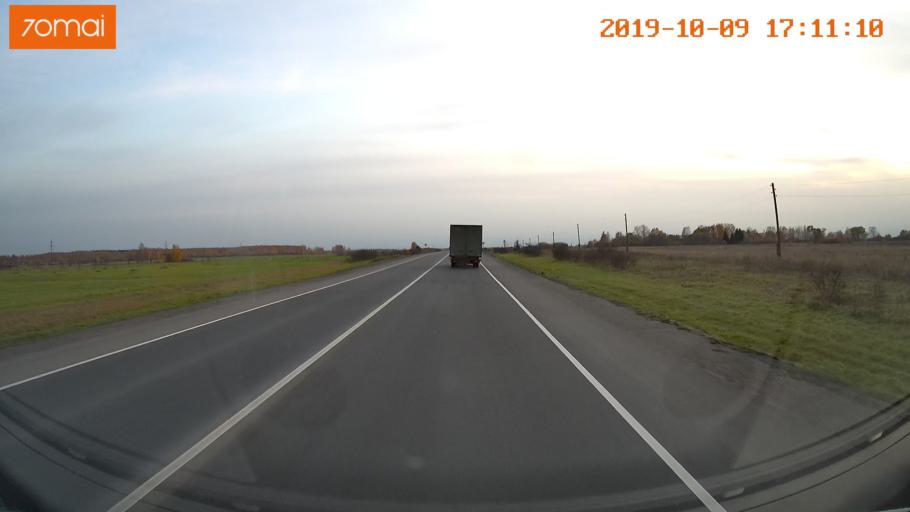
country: RU
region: Ivanovo
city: Privolzhsk
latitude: 57.3467
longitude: 41.2522
